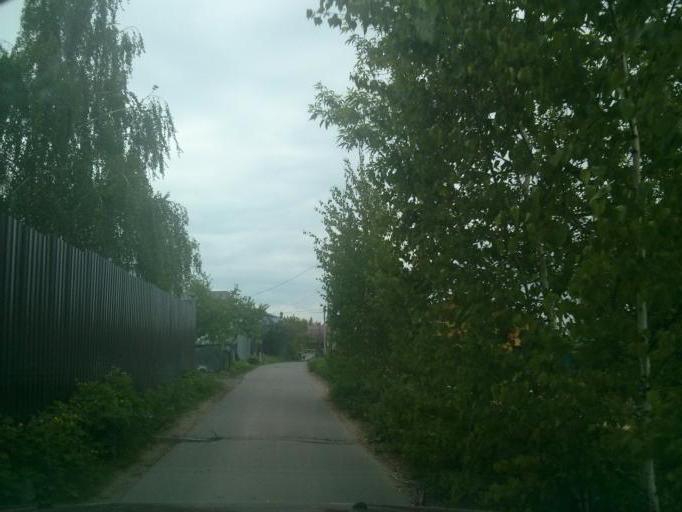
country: RU
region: Nizjnij Novgorod
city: Afonino
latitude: 56.2993
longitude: 44.0998
